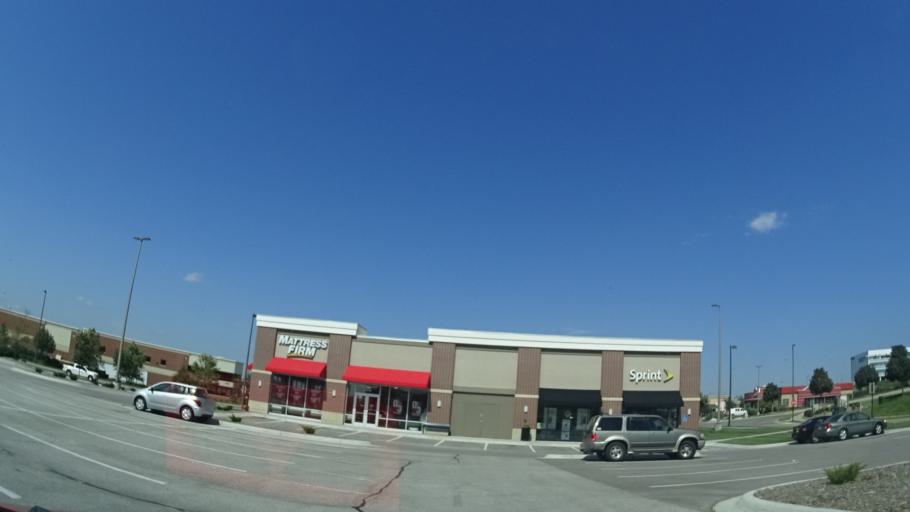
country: US
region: Nebraska
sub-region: Sarpy County
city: Papillion
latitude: 41.1340
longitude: -96.0254
